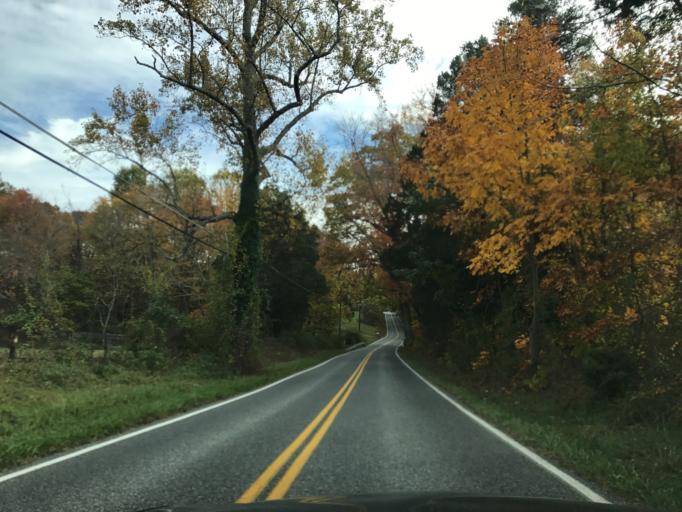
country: US
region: Maryland
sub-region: Harford County
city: Pleasant Hills
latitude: 39.4617
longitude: -76.3790
